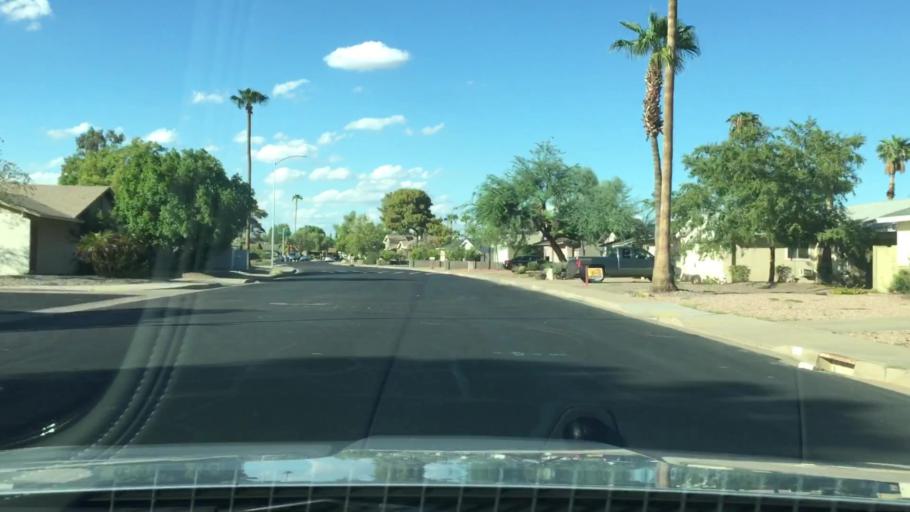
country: US
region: Arizona
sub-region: Maricopa County
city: San Carlos
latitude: 33.3608
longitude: -111.8726
